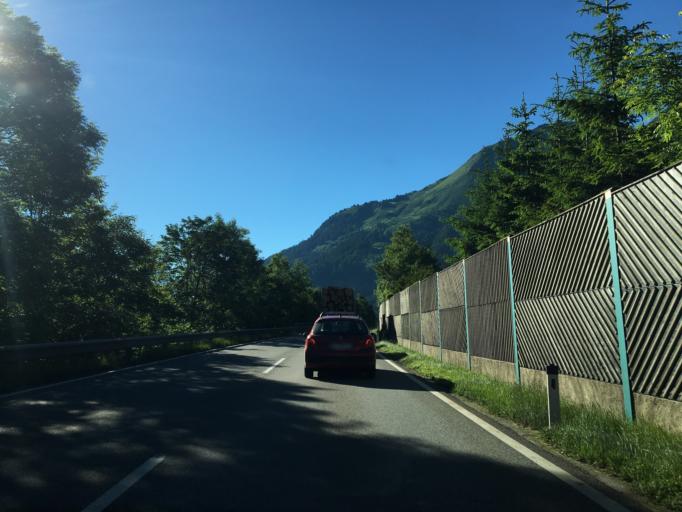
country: AT
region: Tyrol
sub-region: Politischer Bezirk Reutte
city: Bichlbach
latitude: 47.4219
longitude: 10.7909
